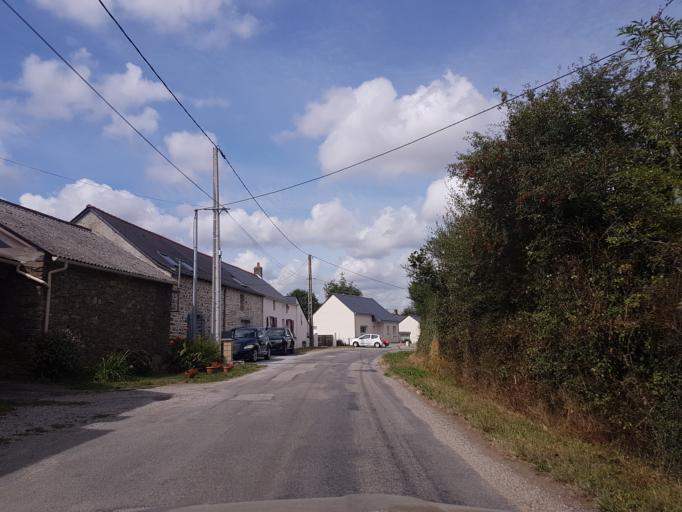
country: FR
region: Pays de la Loire
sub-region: Departement de la Loire-Atlantique
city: Petit-Mars
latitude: 47.4022
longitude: -1.4291
